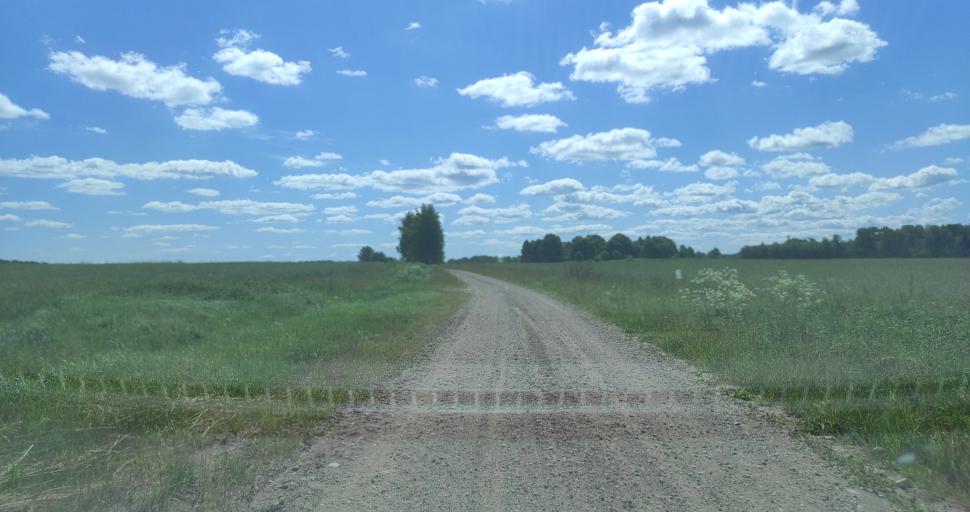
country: LV
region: Aizpute
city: Aizpute
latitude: 56.8630
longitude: 21.7014
